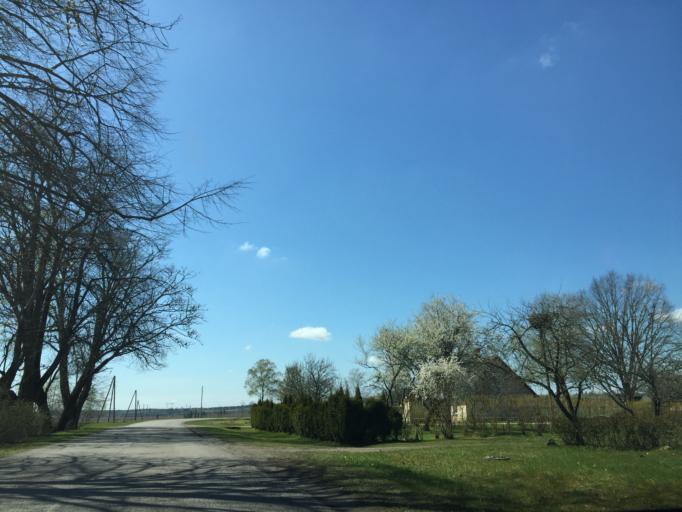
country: LV
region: Strenci
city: Seda
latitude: 57.5765
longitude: 25.7689
